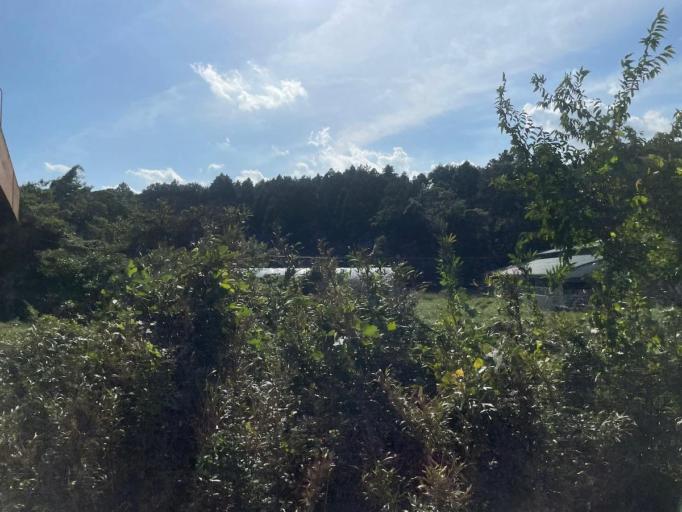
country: JP
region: Mie
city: Komono
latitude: 35.0036
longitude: 136.5268
